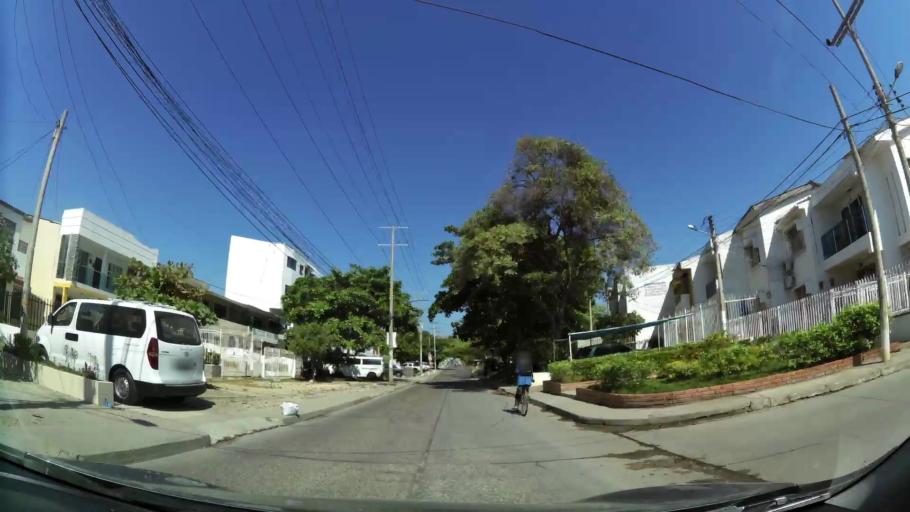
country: CO
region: Bolivar
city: Cartagena
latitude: 10.3914
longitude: -75.5064
